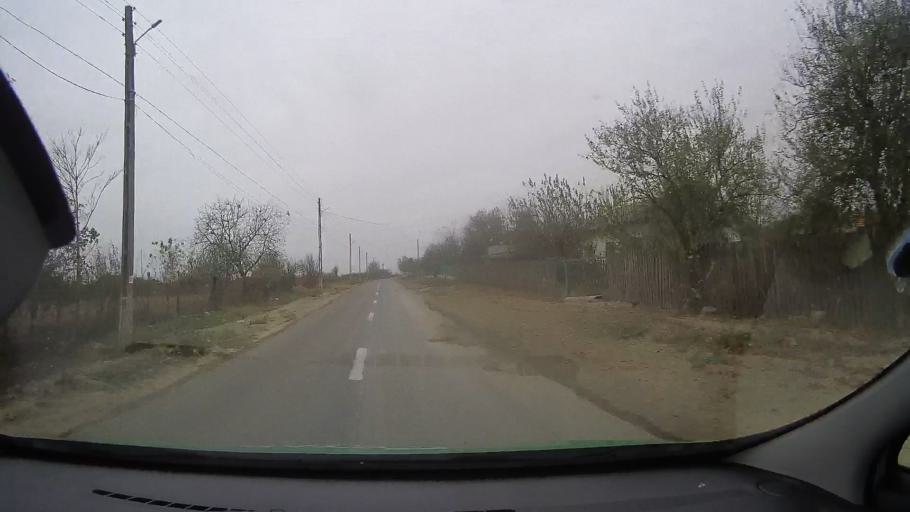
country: RO
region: Constanta
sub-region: Comuna Vulturu
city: Vulturu
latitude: 44.6536
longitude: 28.2676
